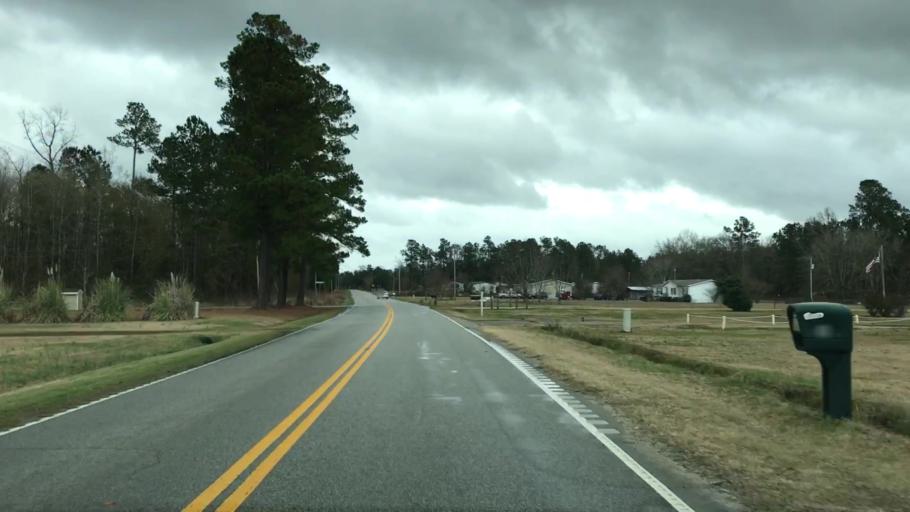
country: US
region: South Carolina
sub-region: Williamsburg County
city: Andrews
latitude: 33.4929
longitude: -79.5057
